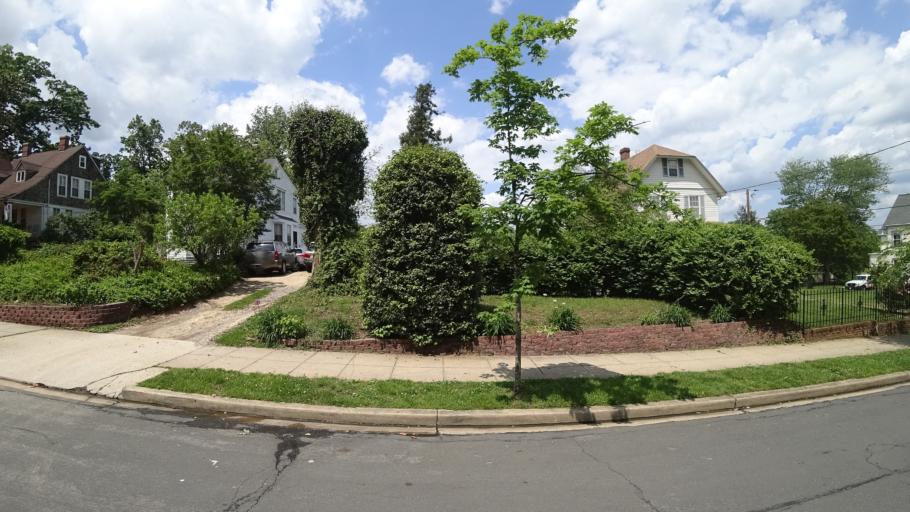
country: US
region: Maryland
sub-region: Prince George's County
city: Mount Rainier
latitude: 38.9338
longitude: -76.9849
